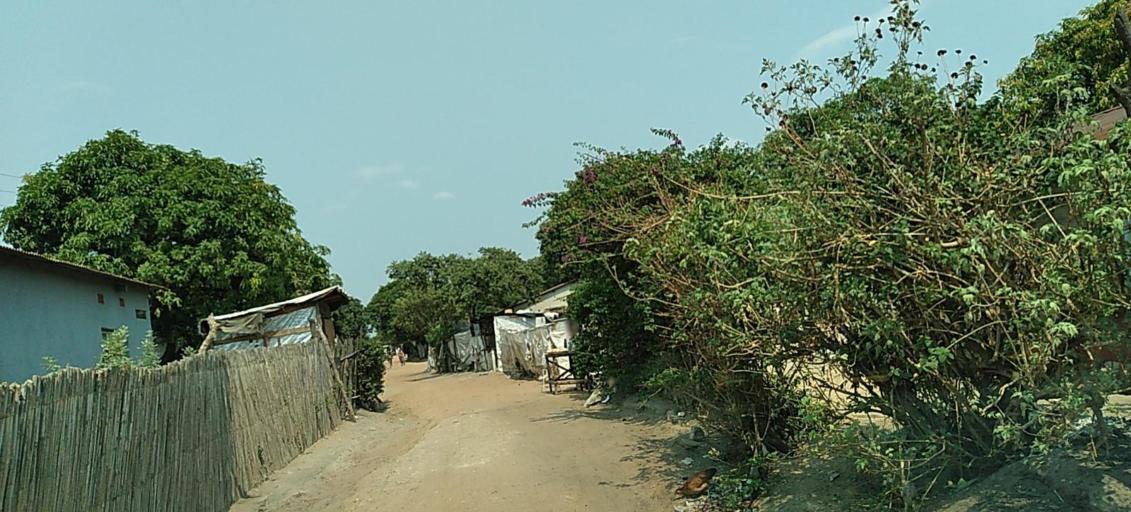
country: ZM
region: Copperbelt
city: Chambishi
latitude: -12.6311
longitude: 28.0730
